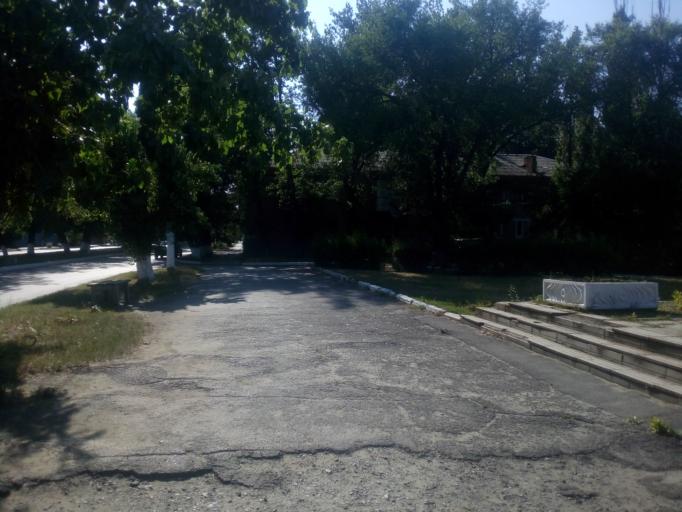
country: RU
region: Rostov
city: Sholokhovskiy
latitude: 48.2821
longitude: 41.0524
